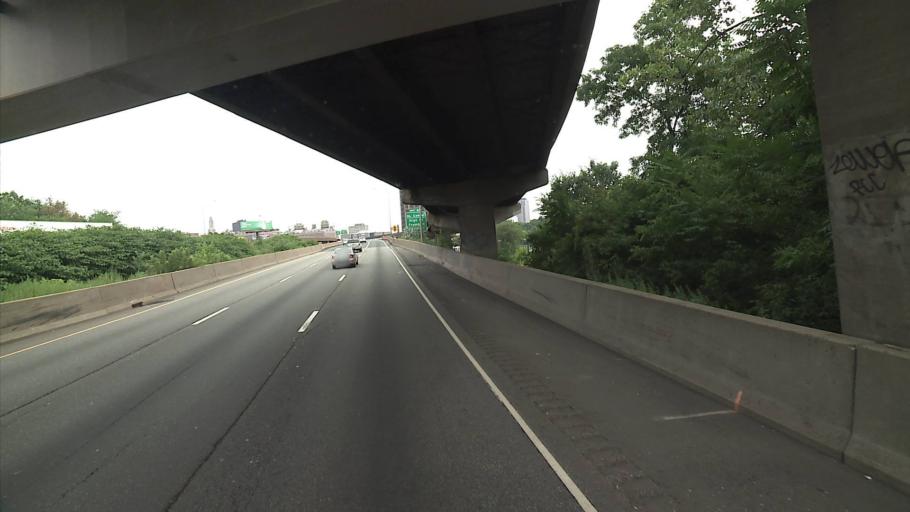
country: US
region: Connecticut
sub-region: Hartford County
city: Hartford
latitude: 41.7610
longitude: -72.6985
